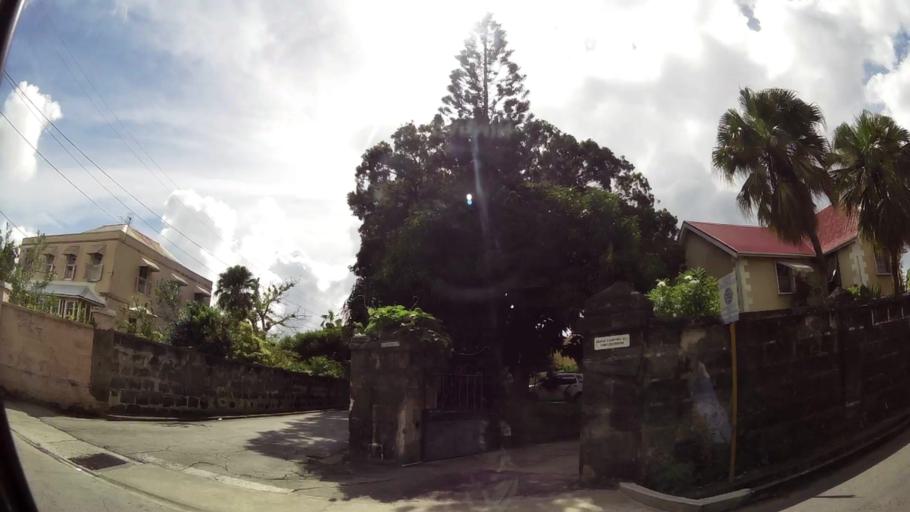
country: BB
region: Saint Michael
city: Bridgetown
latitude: 13.1087
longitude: -59.6134
